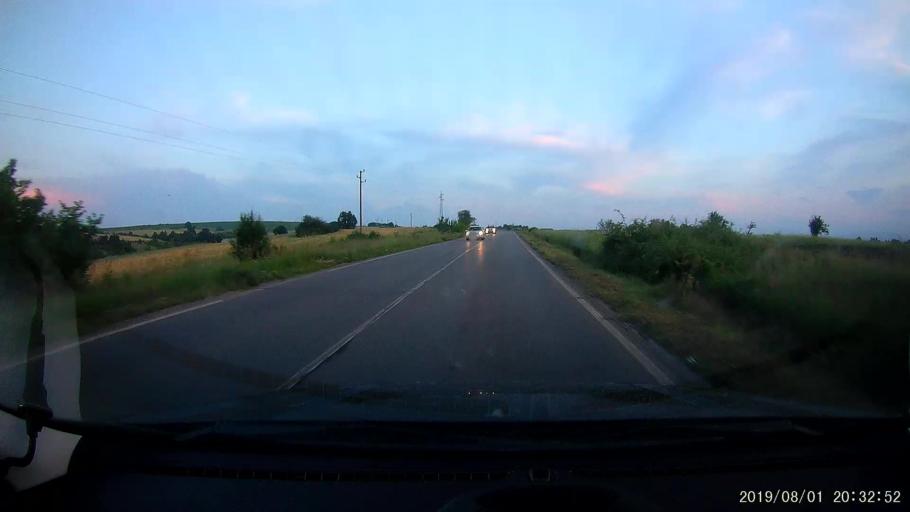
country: BG
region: Yambol
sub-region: Obshtina Elkhovo
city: Elkhovo
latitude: 42.1154
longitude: 26.5311
